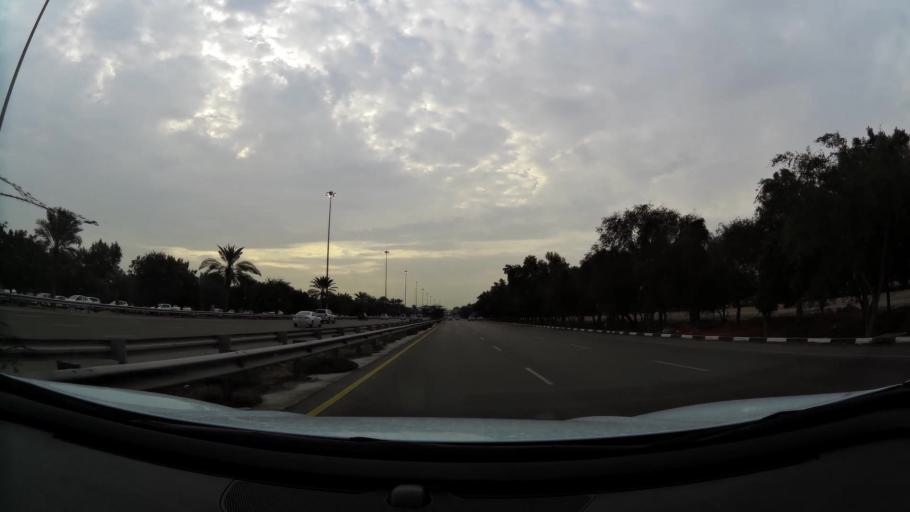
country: AE
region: Abu Dhabi
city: Abu Dhabi
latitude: 24.3677
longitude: 54.5586
